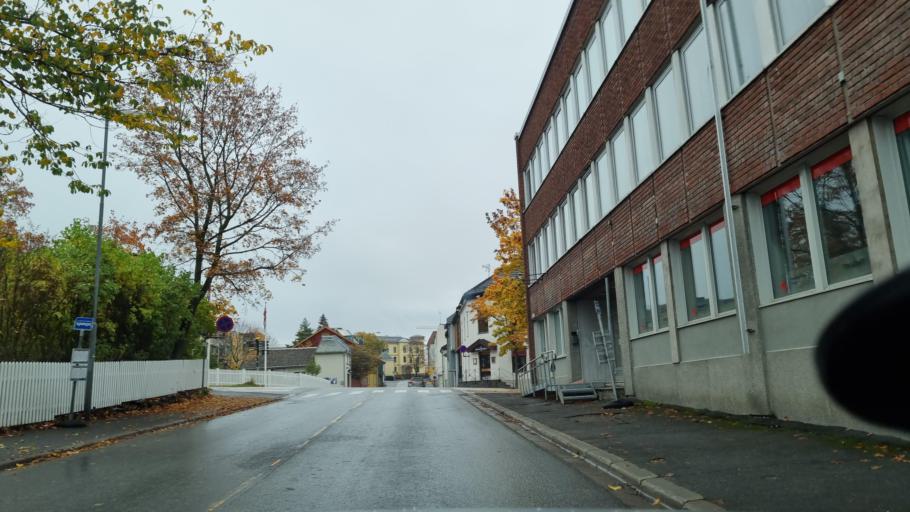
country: NO
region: Hedmark
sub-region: Hamar
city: Hamar
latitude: 60.7959
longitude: 11.0674
